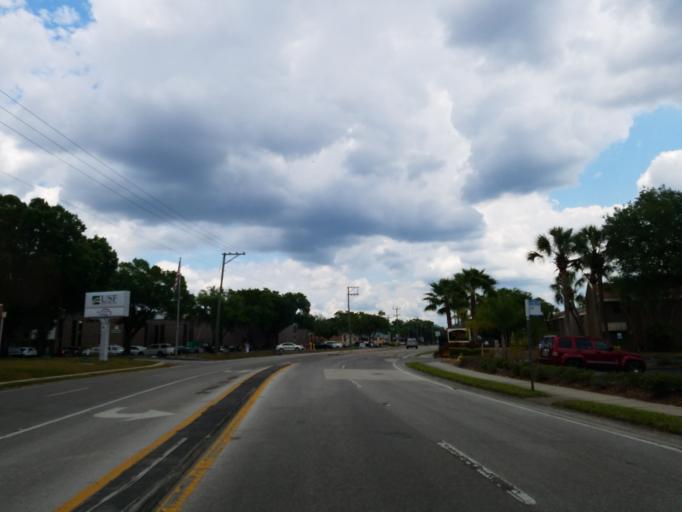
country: US
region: Florida
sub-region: Hillsborough County
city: Brandon
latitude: 27.9341
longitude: -82.2962
